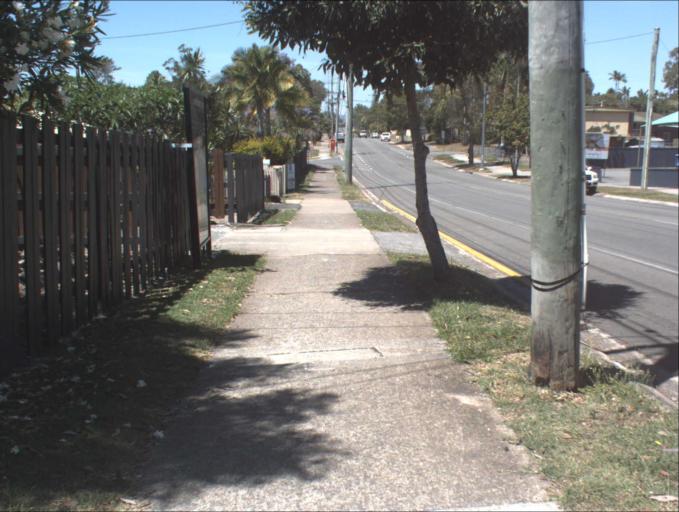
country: AU
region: Queensland
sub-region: Logan
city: Beenleigh
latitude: -27.7071
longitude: 153.2123
